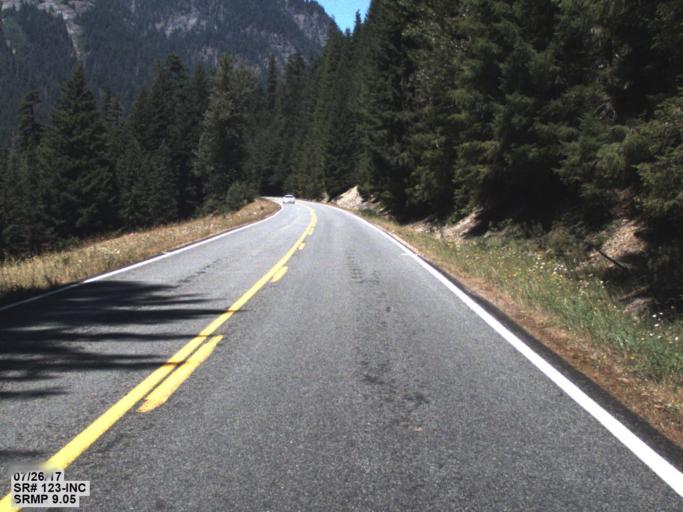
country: US
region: Washington
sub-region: King County
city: Enumclaw
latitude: 46.8046
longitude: -121.5547
